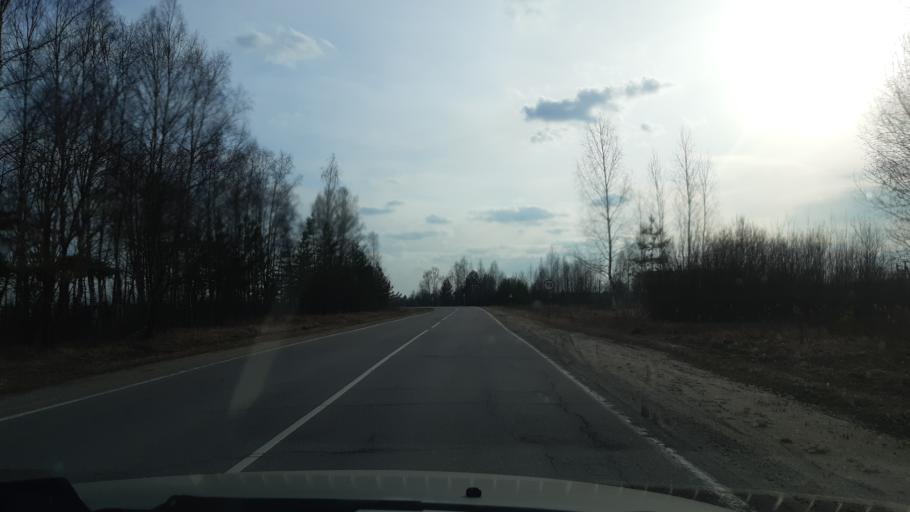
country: RU
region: Vladimir
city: Luknovo
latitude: 56.1761
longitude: 42.0054
